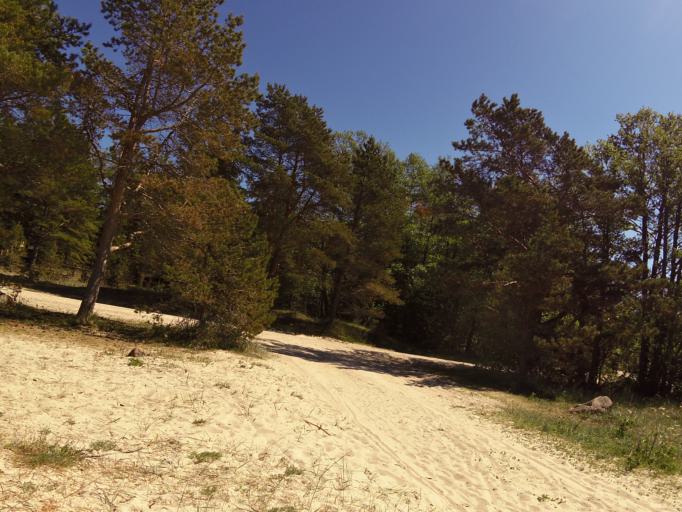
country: EE
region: Harju
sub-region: Paldiski linn
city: Paldiski
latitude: 59.2740
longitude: 23.7784
